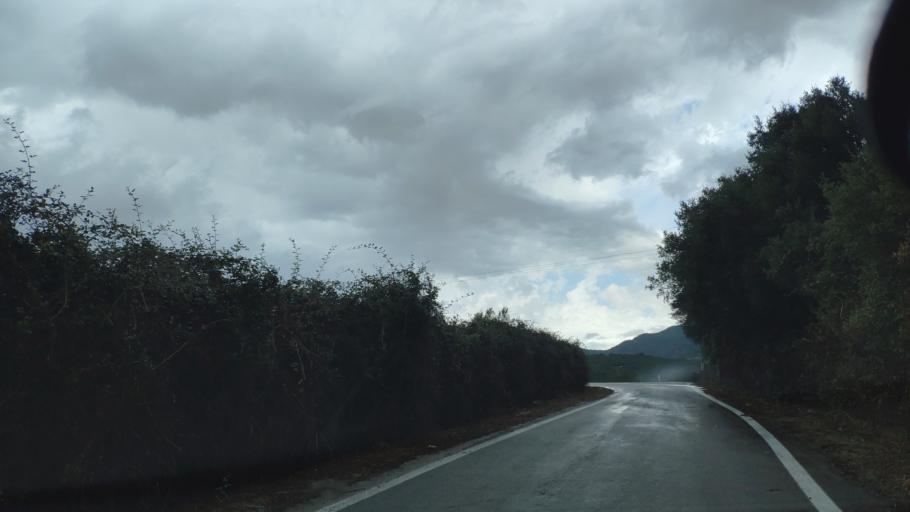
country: GR
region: Central Greece
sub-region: Nomos Evrytanias
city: Kerasochori
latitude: 39.1031
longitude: 21.4277
